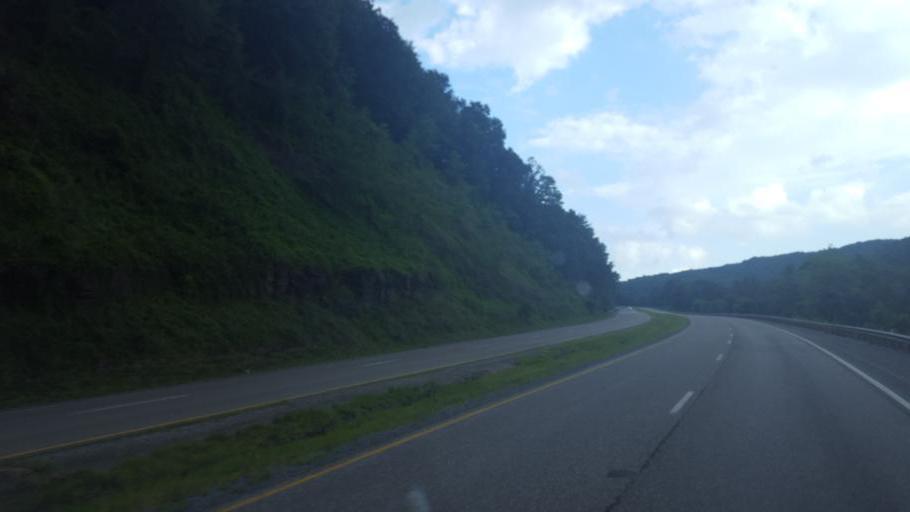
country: US
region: Virginia
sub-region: Wise County
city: Wise
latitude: 37.0354
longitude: -82.5983
